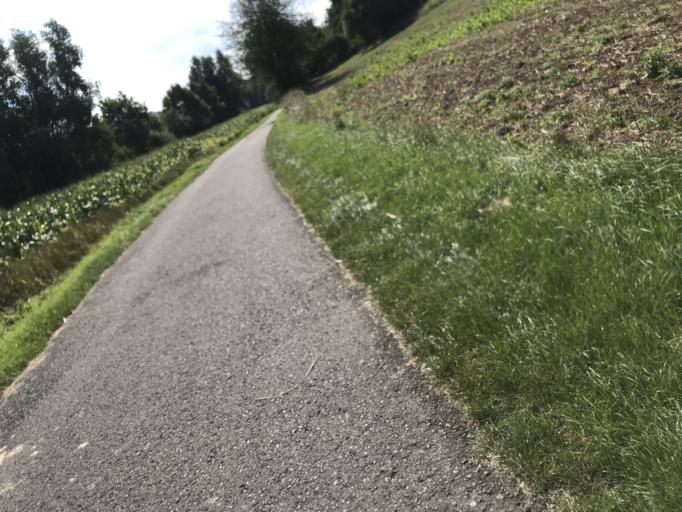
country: DE
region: Hesse
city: Witzenhausen
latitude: 51.3462
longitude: 9.8734
